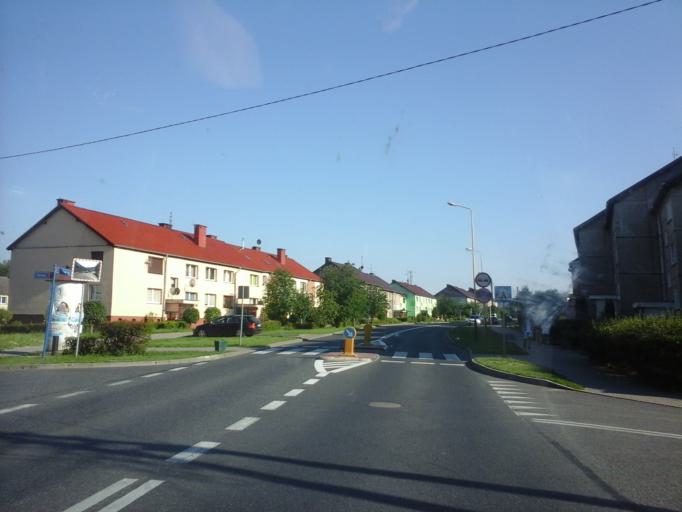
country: PL
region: West Pomeranian Voivodeship
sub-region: Powiat stargardzki
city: Chociwel
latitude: 53.4626
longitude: 15.3333
